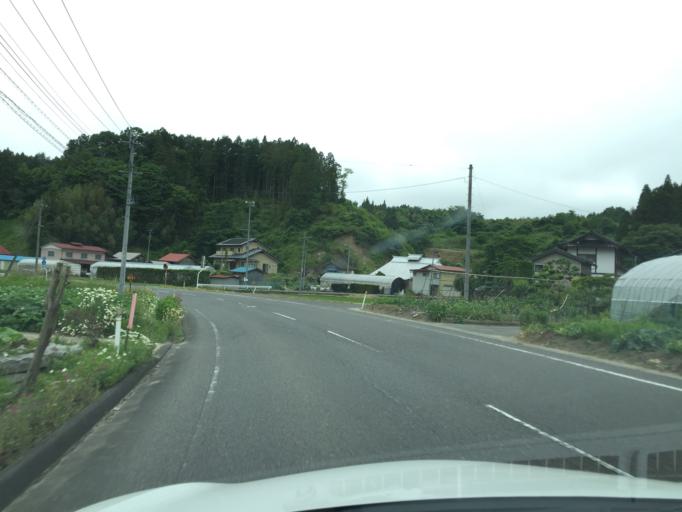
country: JP
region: Fukushima
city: Funehikimachi-funehiki
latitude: 37.3203
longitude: 140.6328
